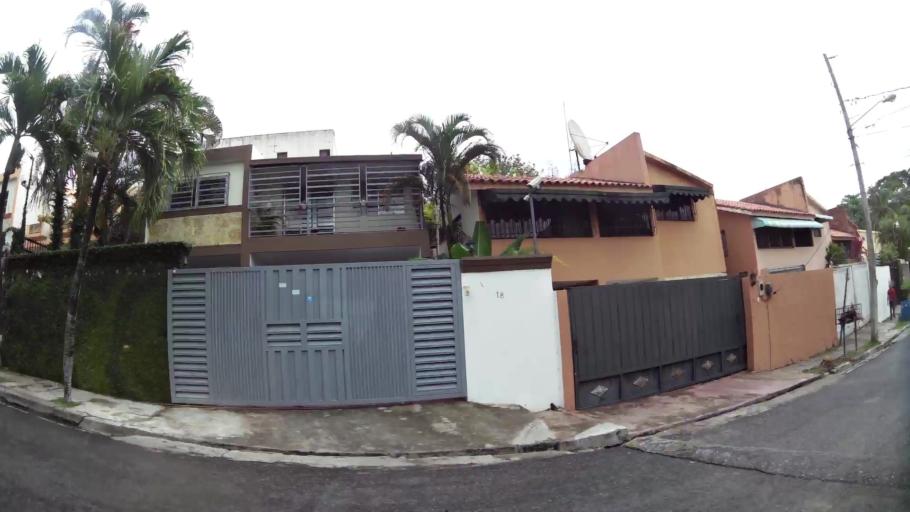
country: DO
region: Nacional
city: La Agustina
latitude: 18.5050
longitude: -69.9365
